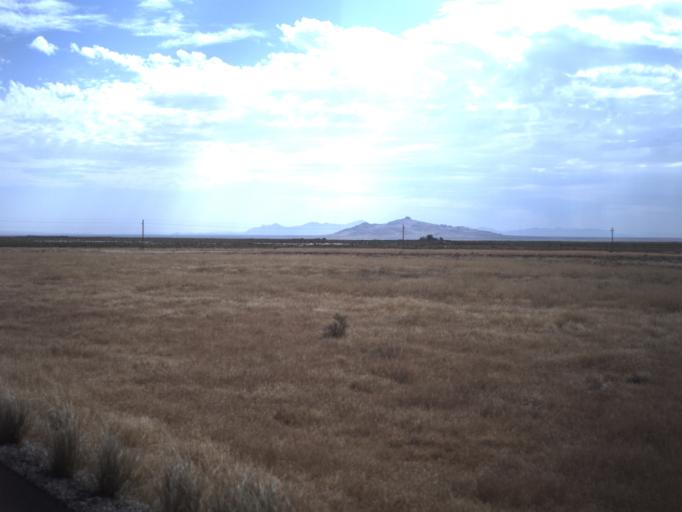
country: US
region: Utah
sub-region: Tooele County
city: Wendover
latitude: 41.4210
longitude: -113.8935
